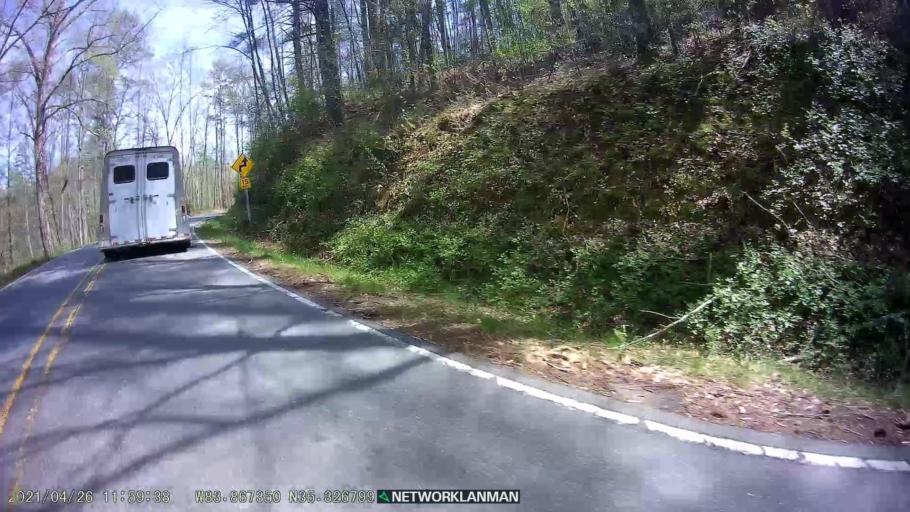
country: US
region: North Carolina
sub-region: Graham County
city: Robbinsville
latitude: 35.3268
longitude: -83.8673
